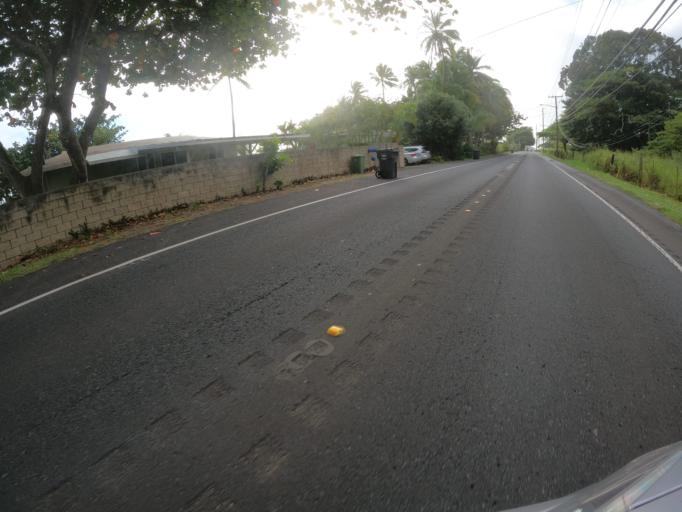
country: US
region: Hawaii
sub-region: Honolulu County
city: Ka'a'awa
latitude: 21.5290
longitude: -157.8355
